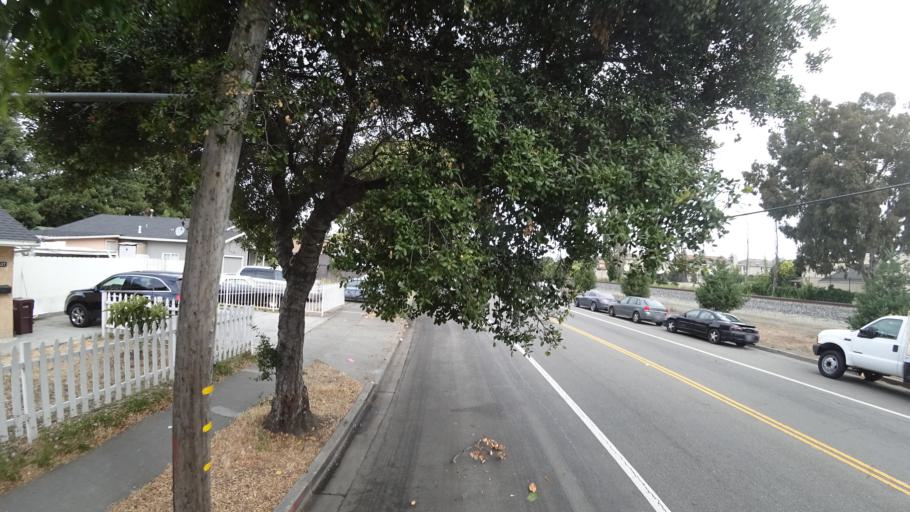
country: US
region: California
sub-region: Alameda County
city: Hayward
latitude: 37.6372
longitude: -122.0671
